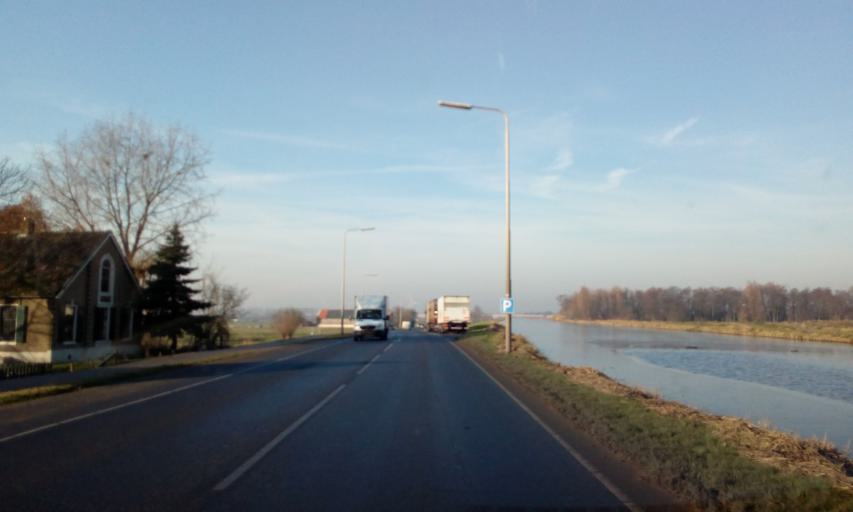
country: NL
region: South Holland
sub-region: Gemeente Gouda
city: Bloemendaal
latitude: 52.0056
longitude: 4.6824
